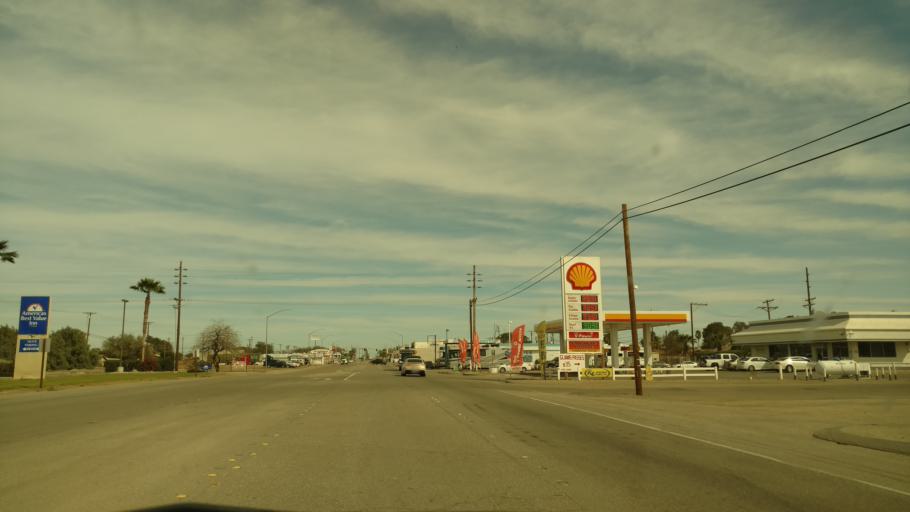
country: US
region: California
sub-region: Imperial County
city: Westmorland
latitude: 33.0373
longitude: -115.6257
